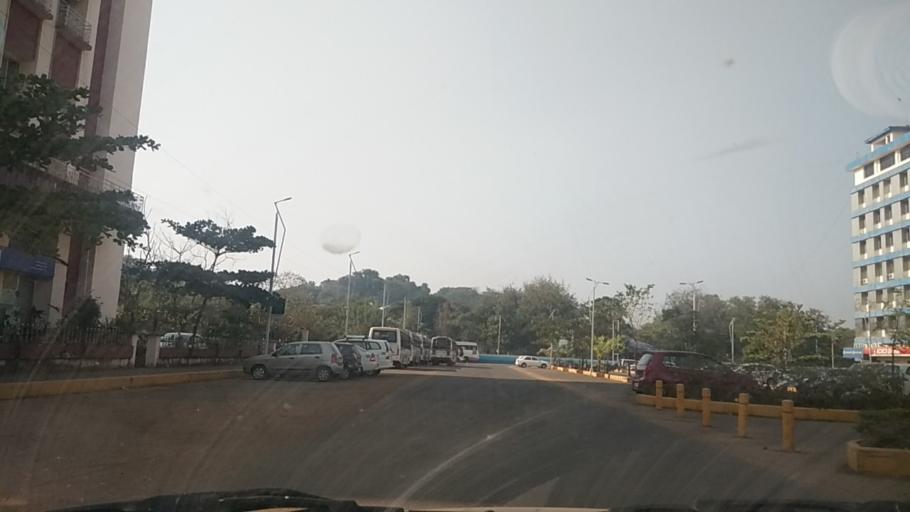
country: IN
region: Goa
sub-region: North Goa
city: Panaji
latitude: 15.4961
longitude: 73.8338
